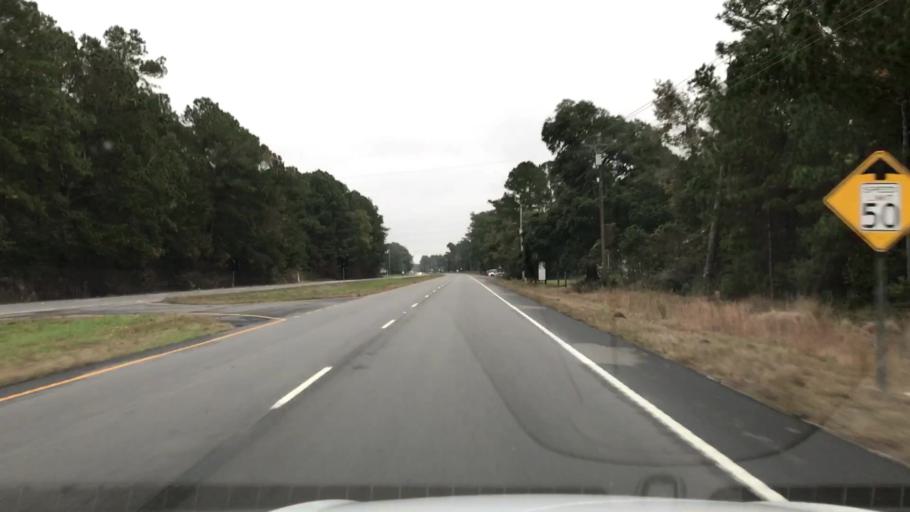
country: US
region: South Carolina
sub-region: Charleston County
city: Awendaw
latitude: 33.0874
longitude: -79.4889
